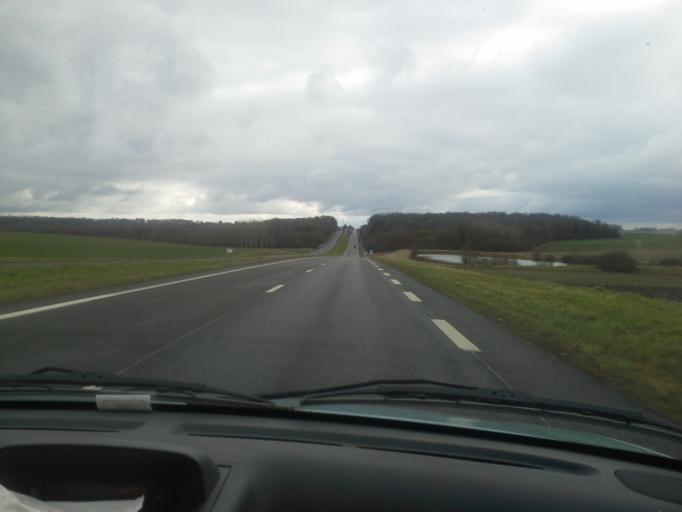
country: FR
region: Centre
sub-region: Departement du Loir-et-Cher
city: Vendome
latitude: 47.7686
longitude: 1.0907
